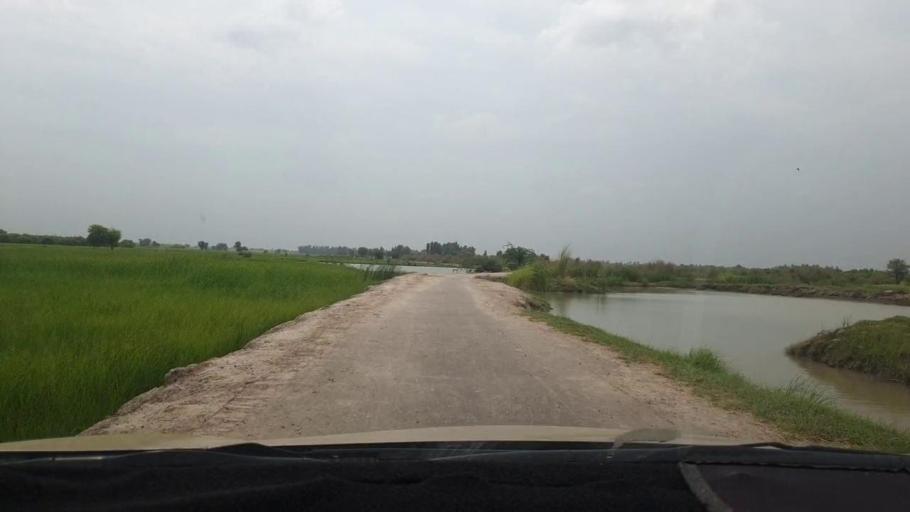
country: PK
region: Sindh
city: Naudero
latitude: 27.6294
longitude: 68.3171
